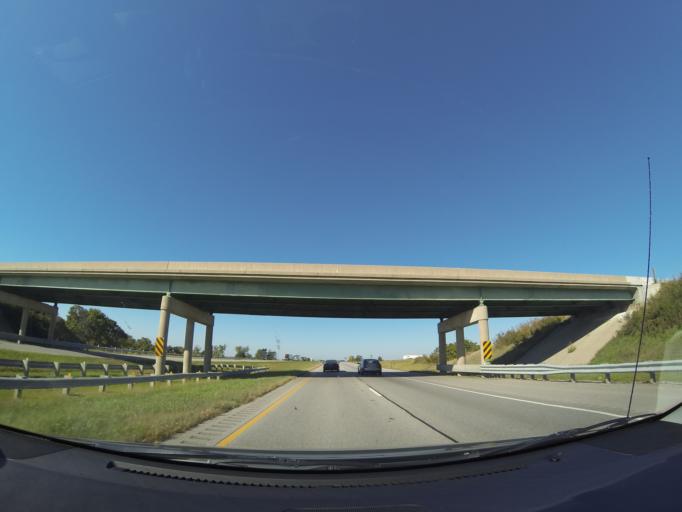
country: US
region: Nebraska
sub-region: Seward County
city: Milford
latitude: 40.8223
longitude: -97.1015
